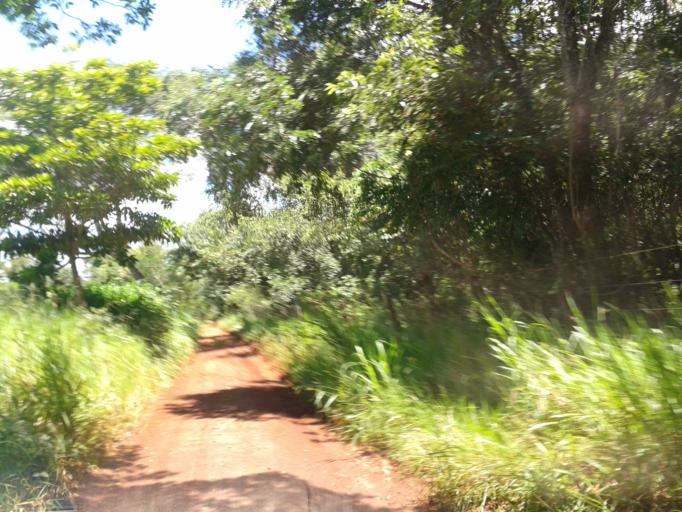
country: BR
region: Minas Gerais
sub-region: Capinopolis
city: Capinopolis
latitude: -18.7936
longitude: -49.8360
